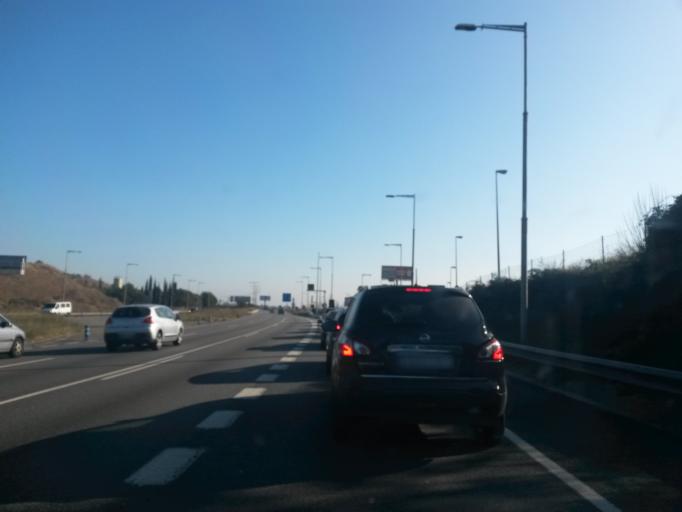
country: ES
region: Catalonia
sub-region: Provincia de Barcelona
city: Santa Coloma de Gramenet
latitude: 41.4615
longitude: 2.2237
